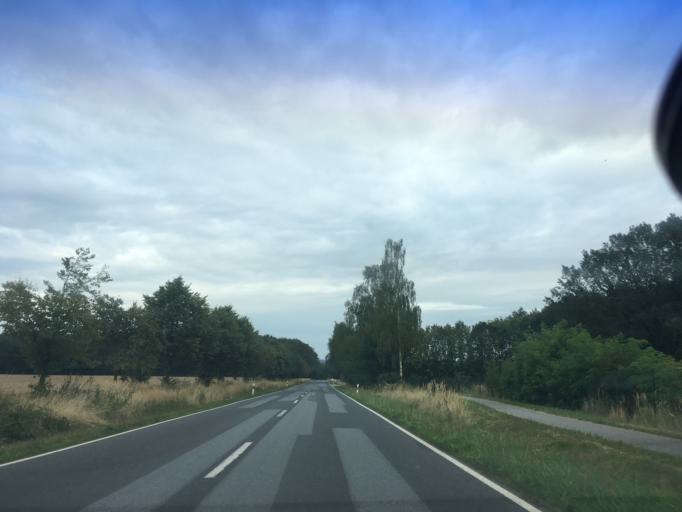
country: DE
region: Saxony
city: Goerlitz
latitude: 51.1192
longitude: 14.9525
